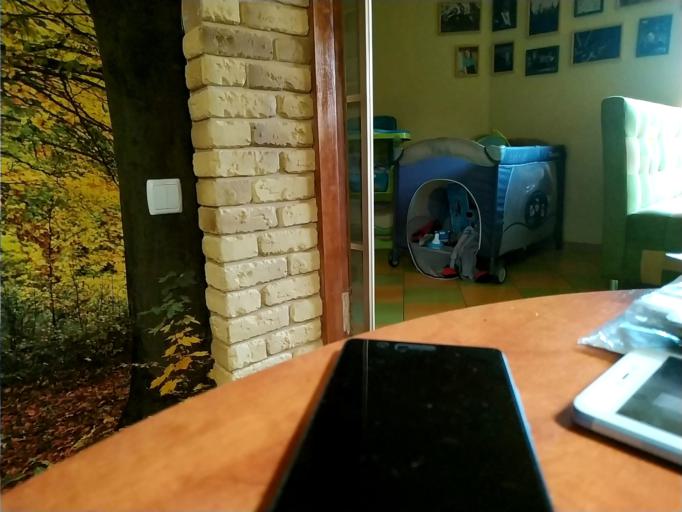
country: RU
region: Kaluga
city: Seredeyskiy
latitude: 53.7988
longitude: 35.3939
